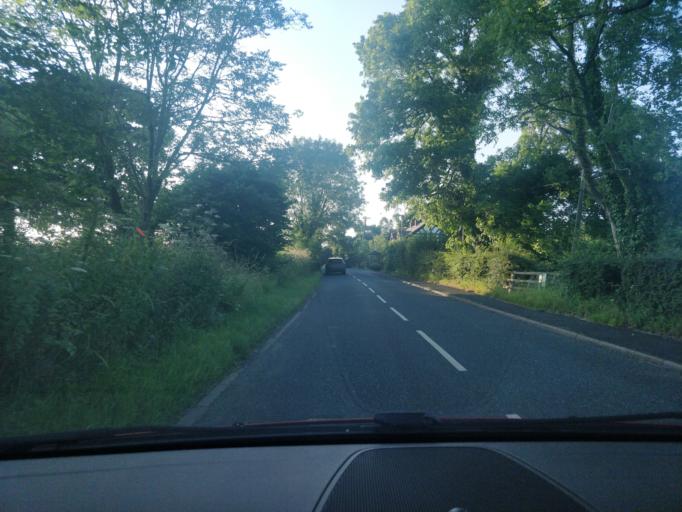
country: GB
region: England
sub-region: Lancashire
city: Parbold
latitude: 53.5795
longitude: -2.7688
